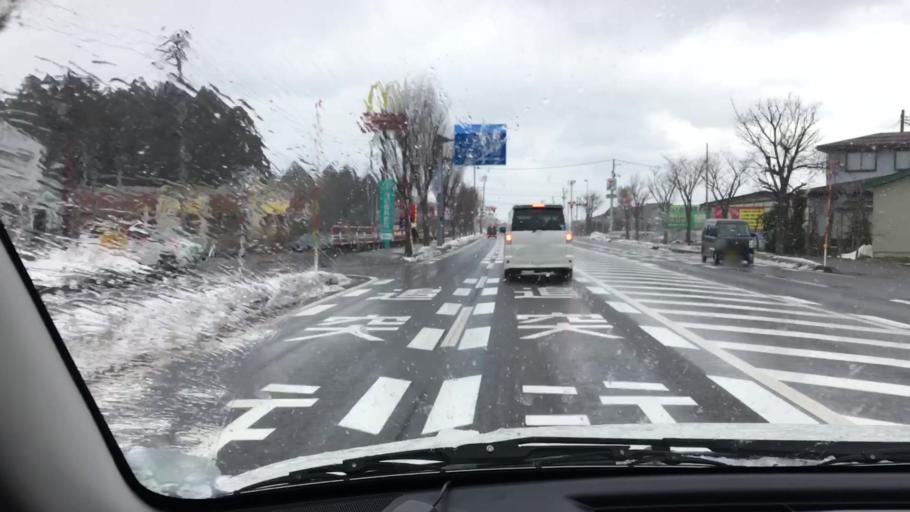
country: JP
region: Niigata
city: Joetsu
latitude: 37.1221
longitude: 138.2324
